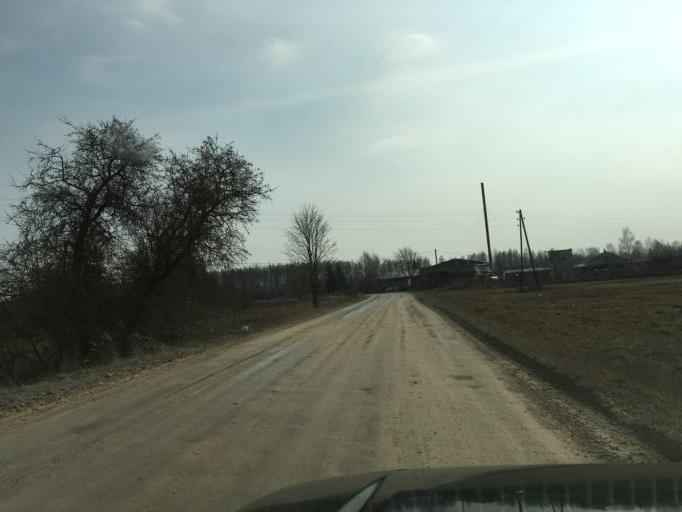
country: LV
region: Olaine
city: Olaine
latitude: 56.7962
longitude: 23.9815
